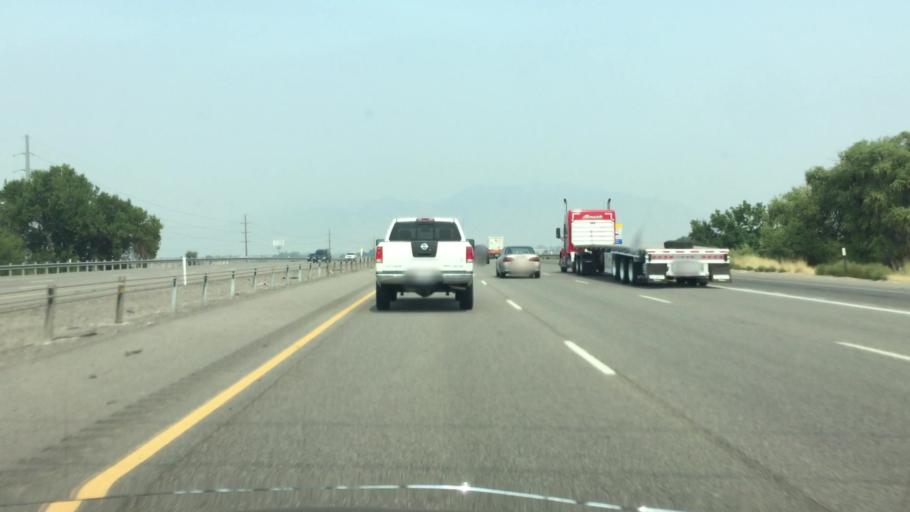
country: US
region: Utah
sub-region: Utah County
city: Payson
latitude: 40.0593
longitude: -111.7288
